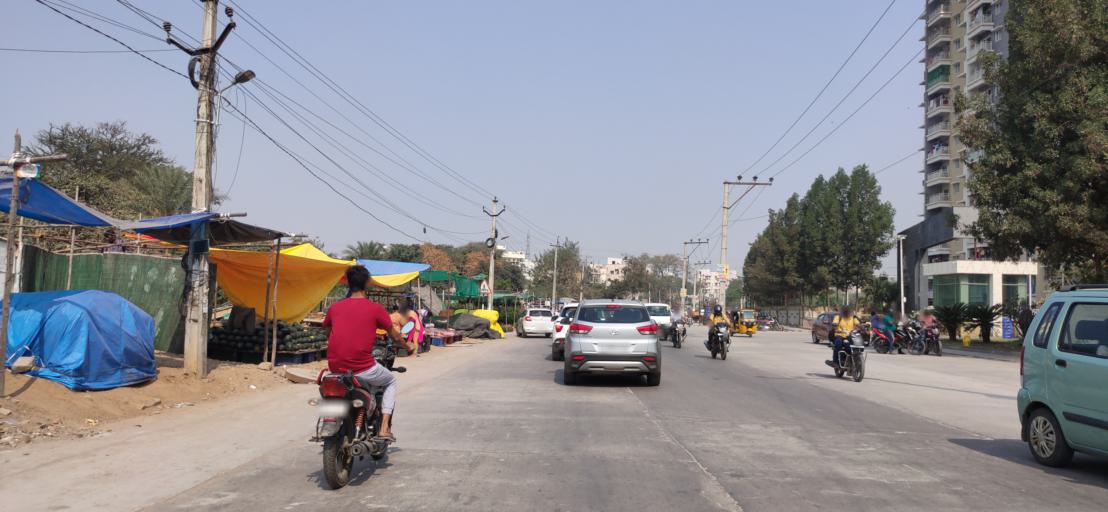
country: IN
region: Telangana
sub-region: Rangareddi
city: Kukatpalli
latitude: 17.5009
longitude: 78.4088
